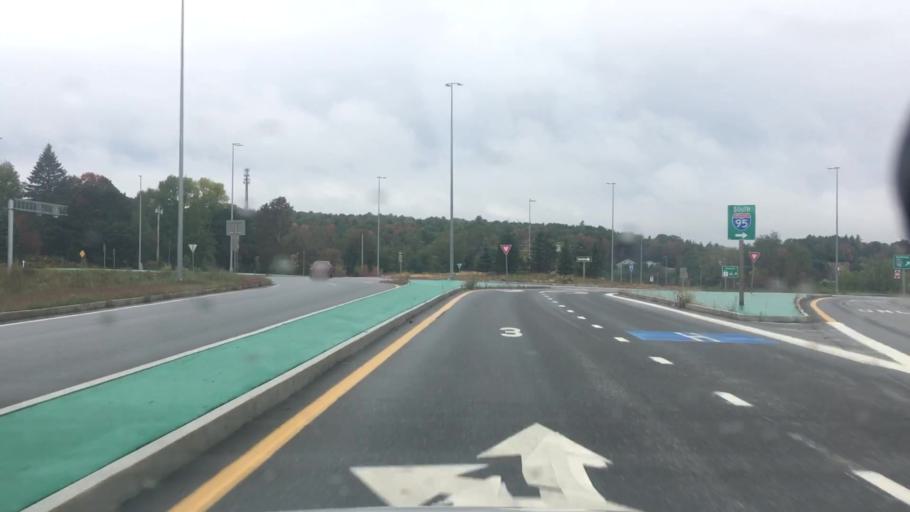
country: US
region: Maine
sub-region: Kennebec County
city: Augusta
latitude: 44.3573
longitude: -69.7841
